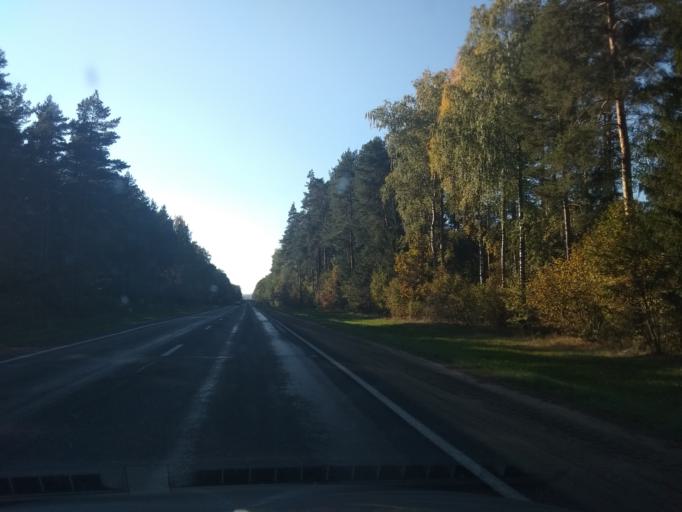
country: BY
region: Grodnenskaya
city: Vawkavysk
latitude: 53.1469
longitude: 24.5220
